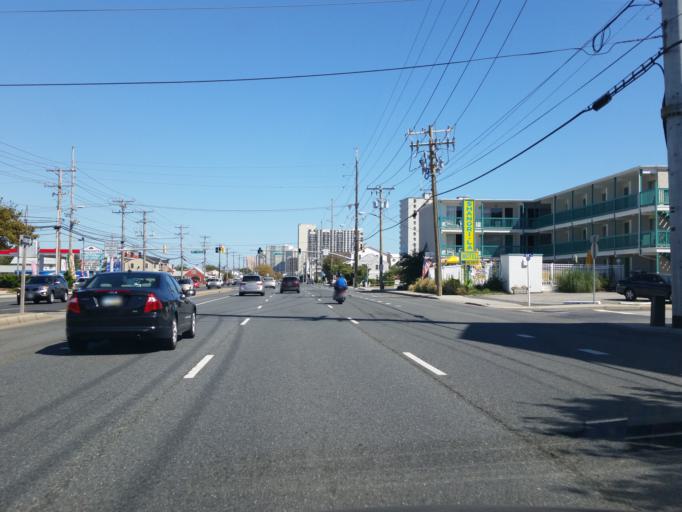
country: US
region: Maryland
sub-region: Worcester County
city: Ocean City
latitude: 38.4024
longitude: -75.0607
